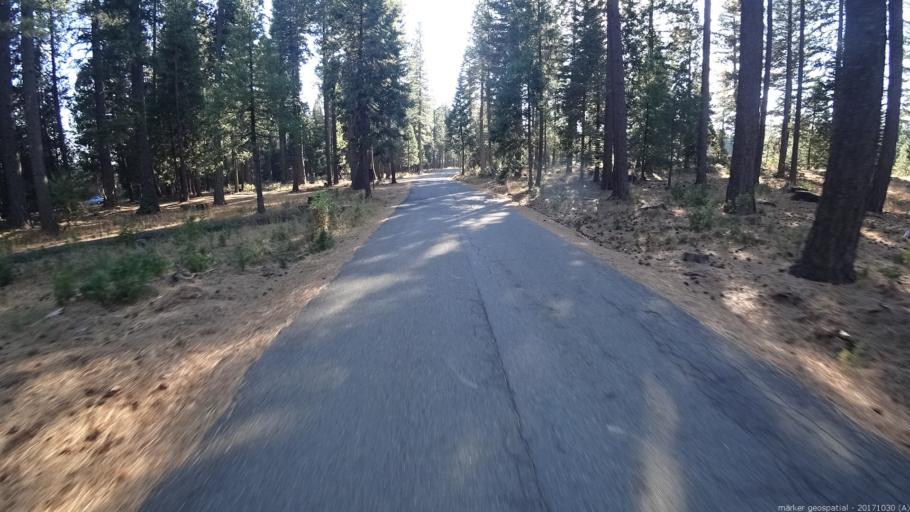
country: US
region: California
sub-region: Shasta County
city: Shingletown
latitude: 40.5422
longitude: -121.7358
